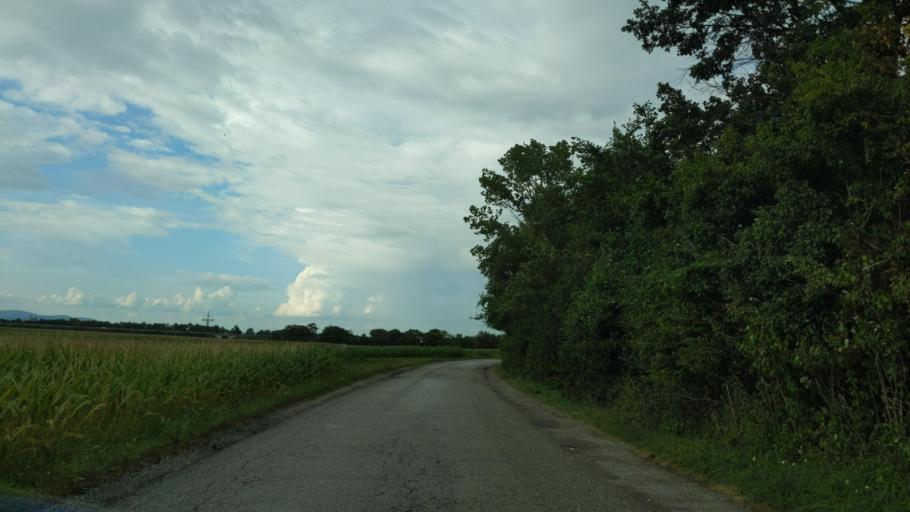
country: AT
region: Lower Austria
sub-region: Politischer Bezirk Wiener Neustadt
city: Katzelsdorf
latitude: 47.7850
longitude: 16.2846
